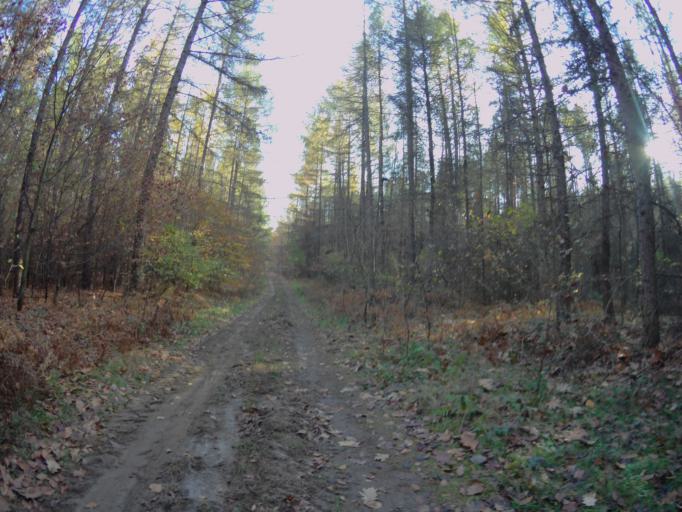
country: PL
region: Subcarpathian Voivodeship
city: Nowa Sarzyna
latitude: 50.3122
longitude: 22.3451
